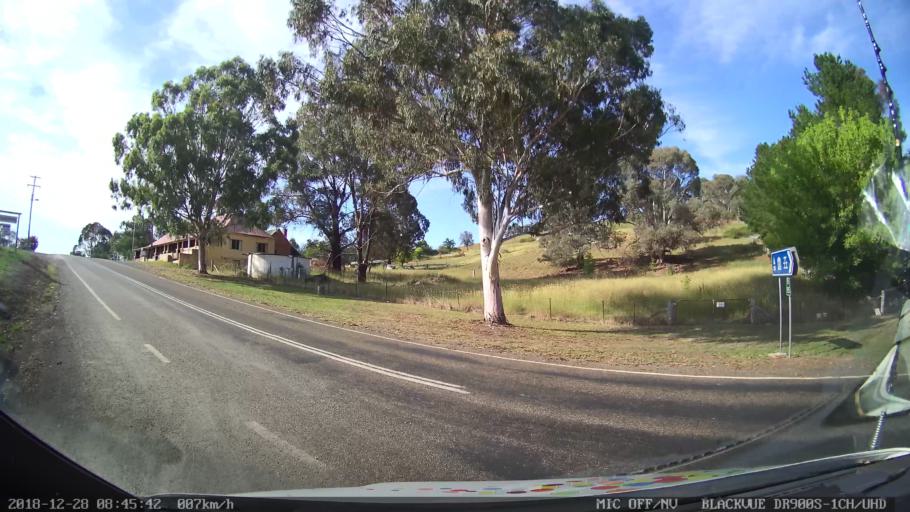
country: AU
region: New South Wales
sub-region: Upper Lachlan Shire
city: Crookwell
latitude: -34.0166
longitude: 149.3285
